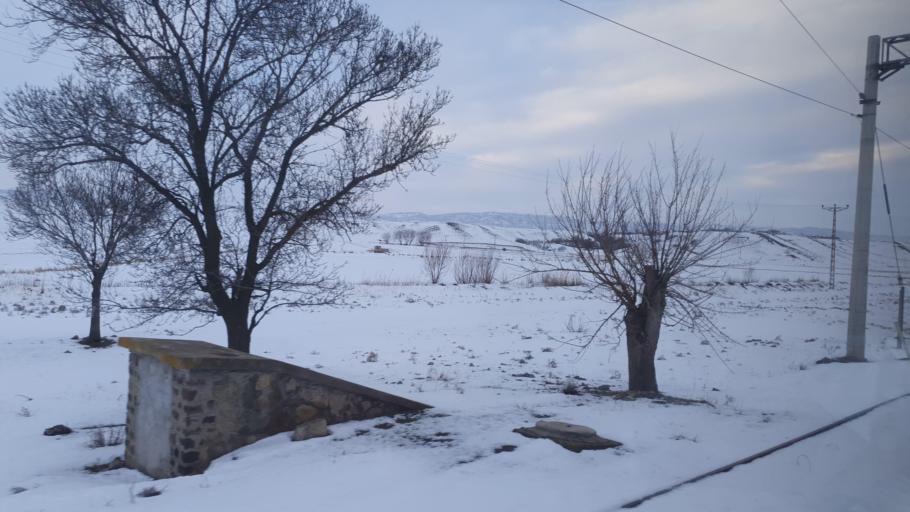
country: TR
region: Kirsehir
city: Mecidiye
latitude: 39.6860
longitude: 34.4005
